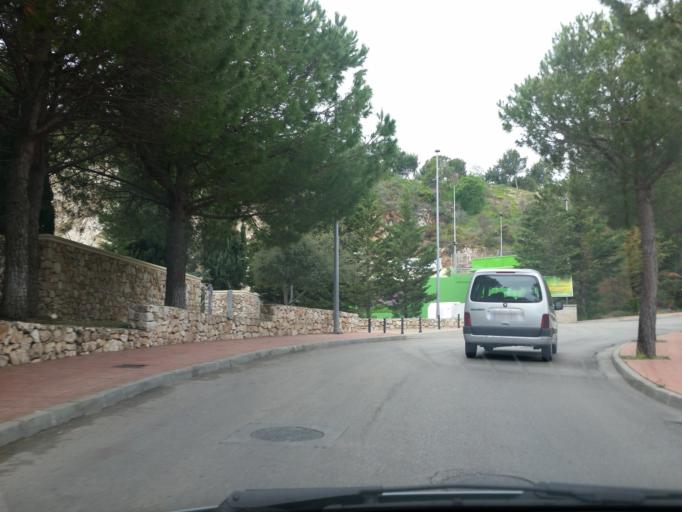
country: ES
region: Andalusia
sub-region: Provincia de Malaga
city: Benalmadena
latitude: 36.6120
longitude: -4.5395
